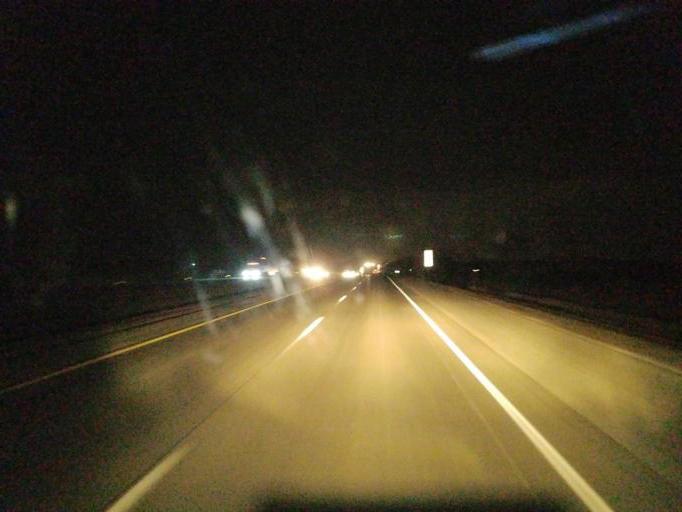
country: US
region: Iowa
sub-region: Dallas County
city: De Soto
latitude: 41.5224
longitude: -94.0648
